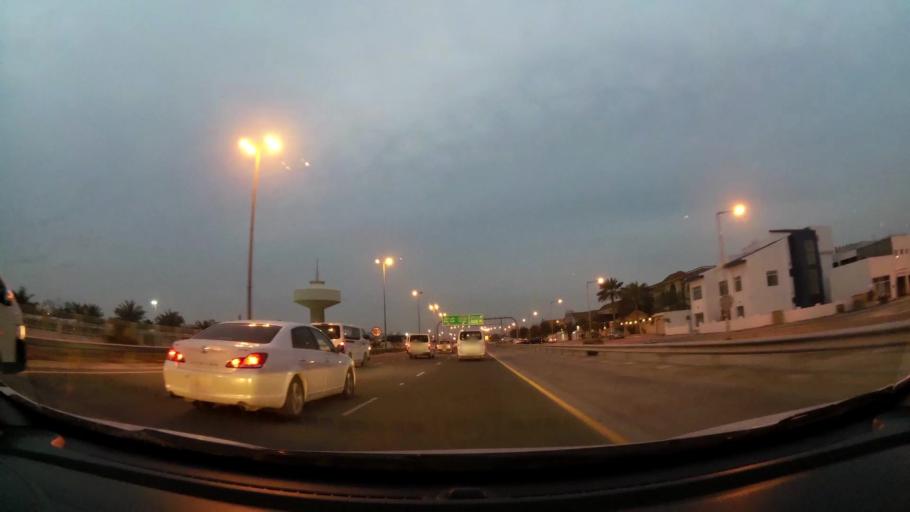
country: BH
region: Northern
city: Madinat `Isa
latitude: 26.1663
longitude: 50.5504
